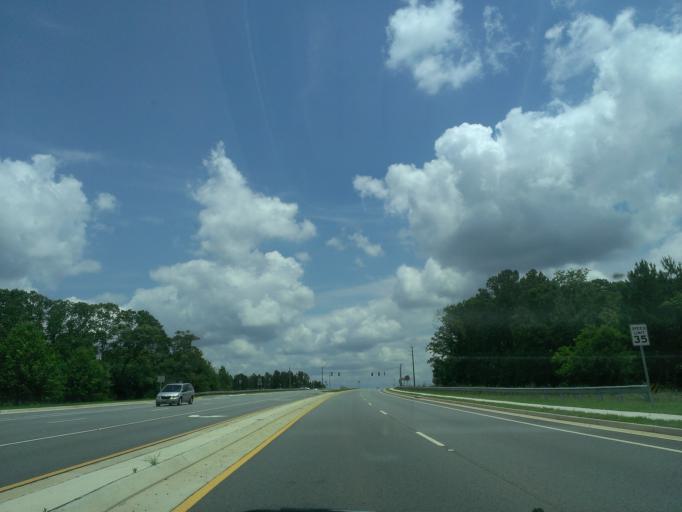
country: US
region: Georgia
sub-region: Oconee County
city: Watkinsville
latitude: 33.9147
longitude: -83.4626
